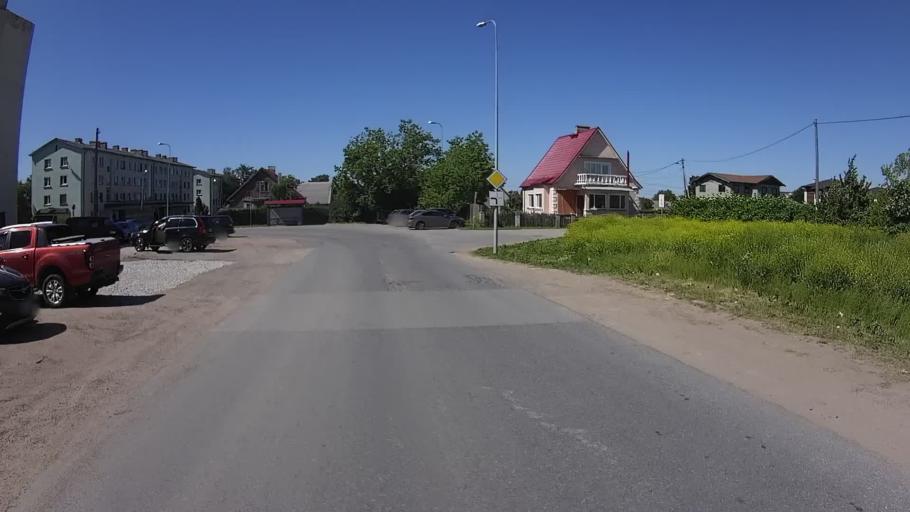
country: EE
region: Ida-Virumaa
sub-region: Kohtla-Jaerve linn
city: Kohtla-Jarve
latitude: 59.4049
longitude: 27.2978
